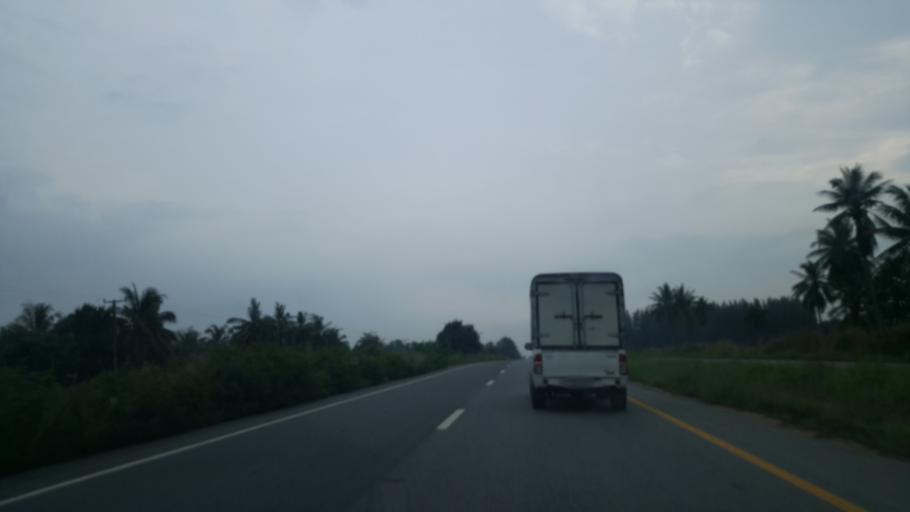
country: TH
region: Rayong
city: Ban Chang
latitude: 12.8024
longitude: 100.9922
